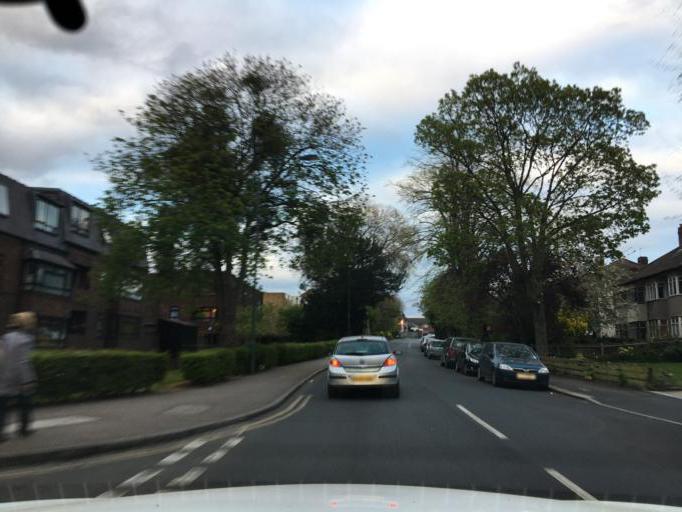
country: GB
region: England
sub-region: Greater London
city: Sidcup
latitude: 51.4285
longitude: 0.0904
